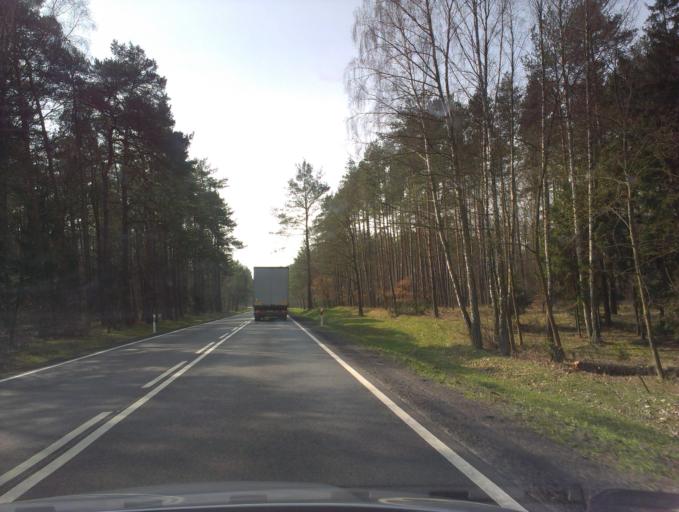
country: PL
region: Greater Poland Voivodeship
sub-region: Powiat zlotowski
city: Okonek
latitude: 53.5117
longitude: 16.8527
